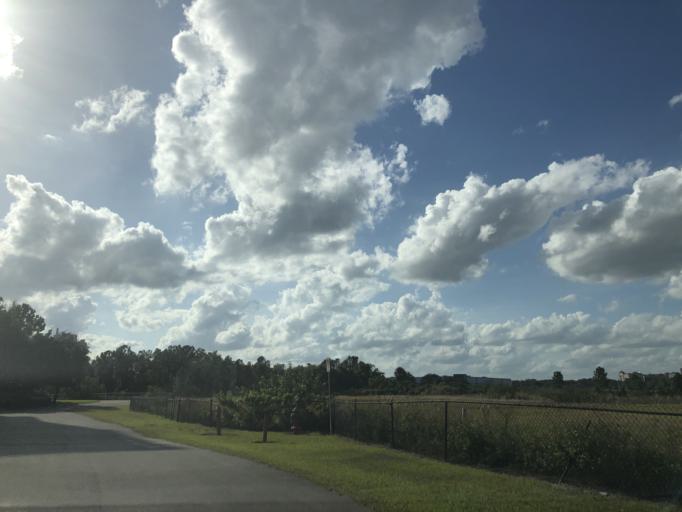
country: US
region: Florida
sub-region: Orange County
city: Tangelo Park
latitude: 28.4347
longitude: -81.4594
